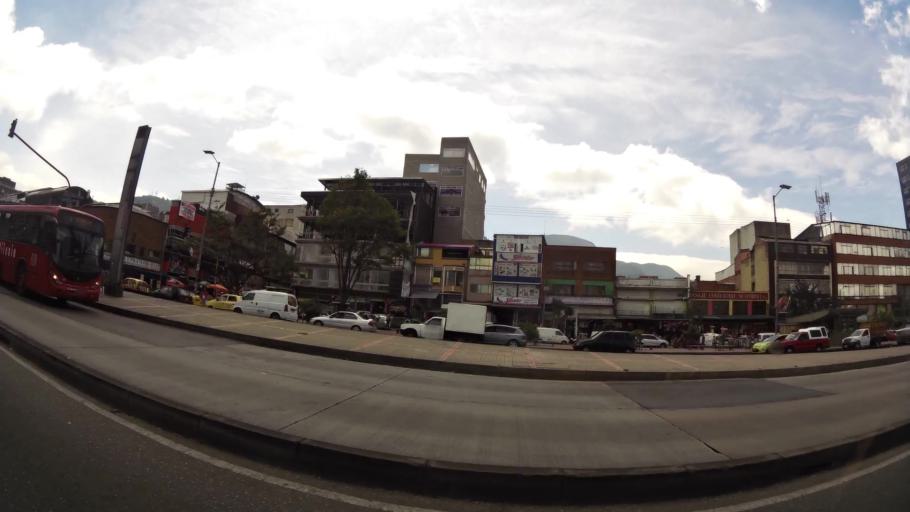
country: CO
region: Bogota D.C.
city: Bogota
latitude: 4.6017
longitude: -74.0812
